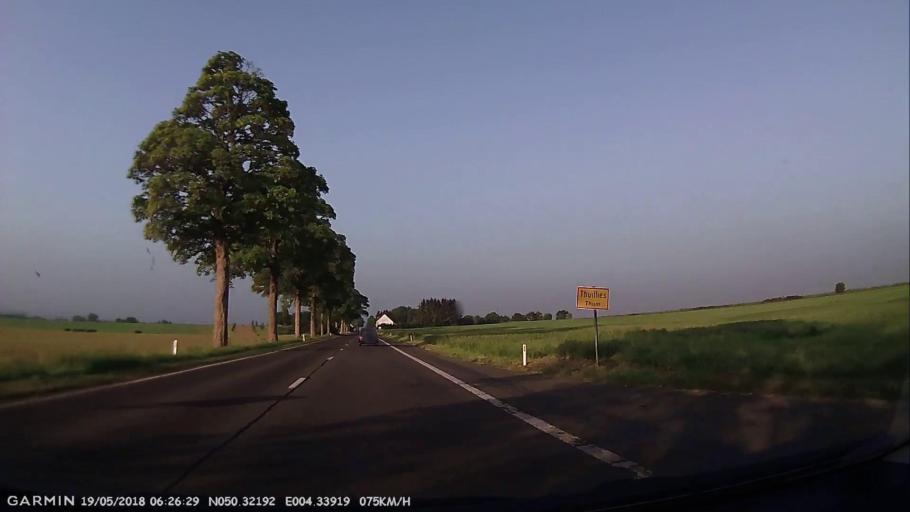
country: BE
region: Wallonia
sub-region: Province du Hainaut
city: Thuin
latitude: 50.3219
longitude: 4.3392
